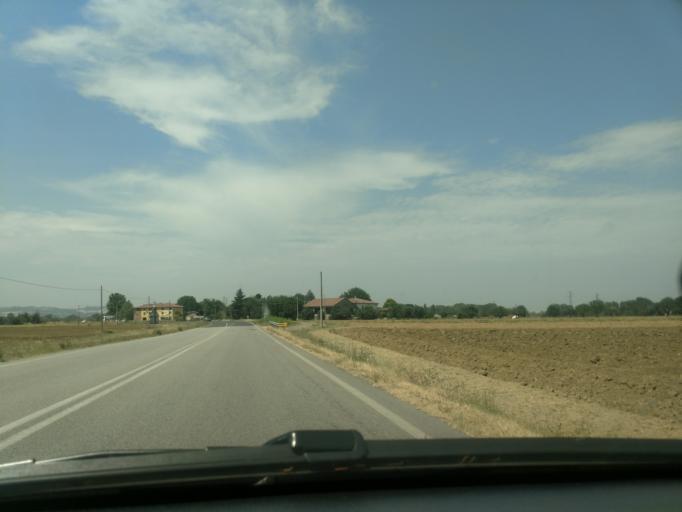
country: IT
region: Emilia-Romagna
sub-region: Provincia di Bologna
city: Villanova
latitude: 44.4837
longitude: 11.4527
